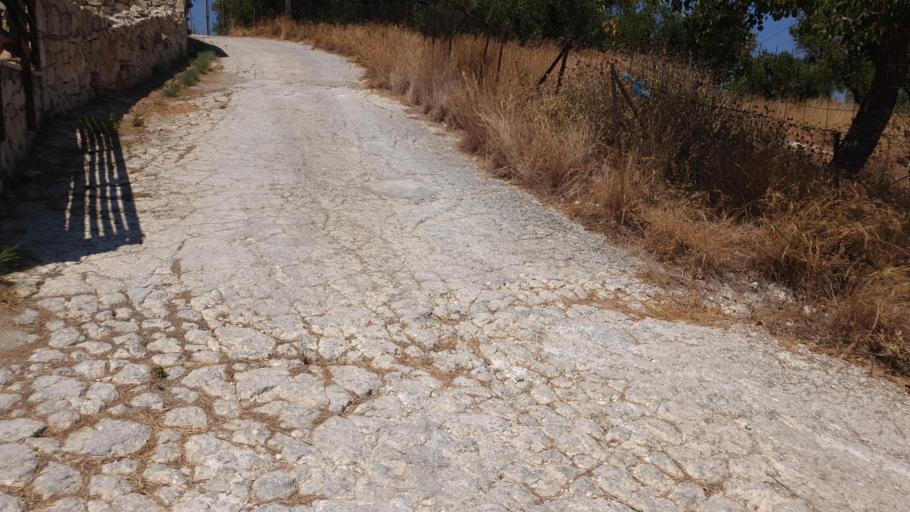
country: GR
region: Ionian Islands
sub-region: Nomos Zakynthou
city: Zakynthos
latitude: 37.7473
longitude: 20.9469
